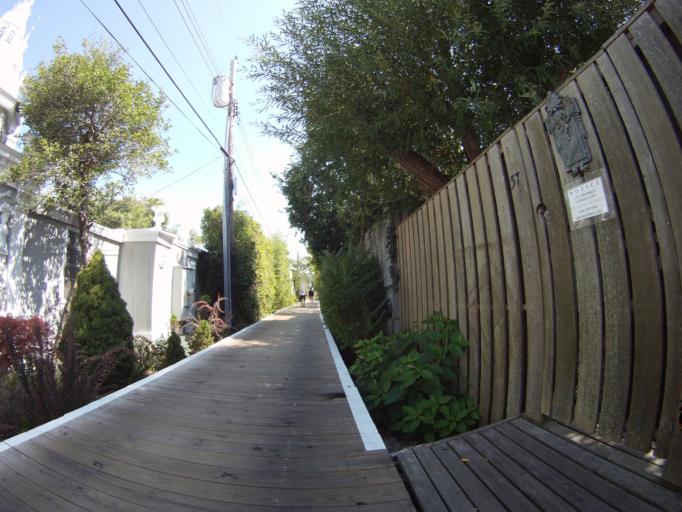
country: US
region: New York
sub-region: Suffolk County
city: West Sayville
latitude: 40.6614
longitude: -73.0853
